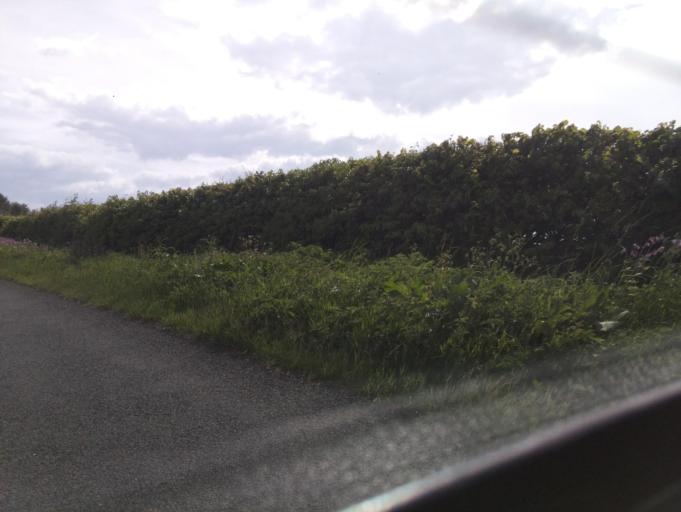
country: GB
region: England
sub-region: Northumberland
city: Alnwick
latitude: 55.4590
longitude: -1.7153
